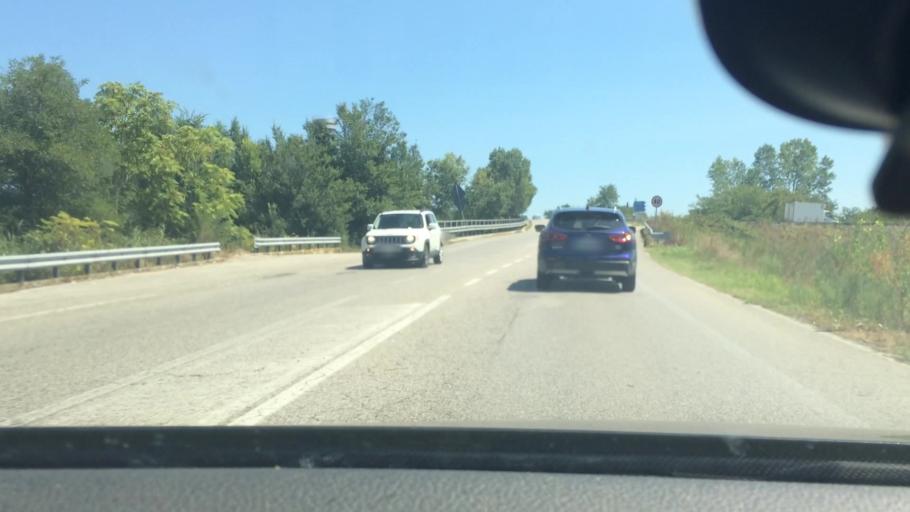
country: IT
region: Emilia-Romagna
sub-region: Provincia di Ferrara
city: Porto Garibaldi
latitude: 44.6889
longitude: 12.2206
